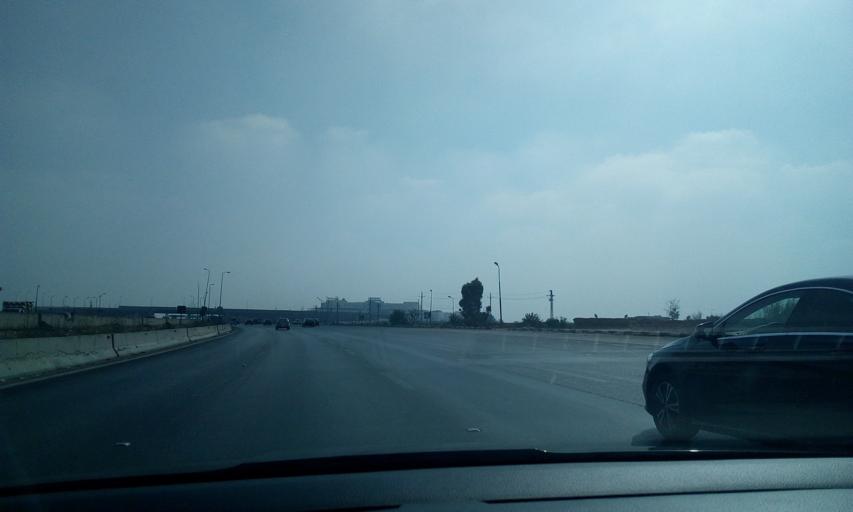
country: EG
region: Eastern Province
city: Bilbays
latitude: 30.1902
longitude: 31.6465
